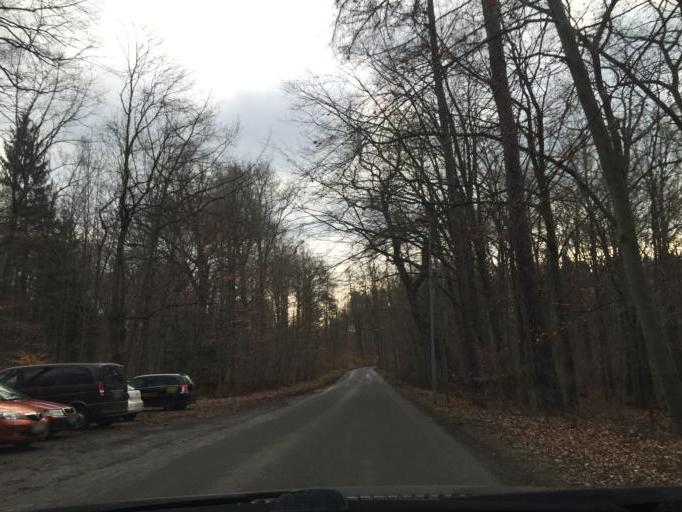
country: DE
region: Saxony
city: Moritzburg
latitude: 51.1758
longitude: 13.6773
